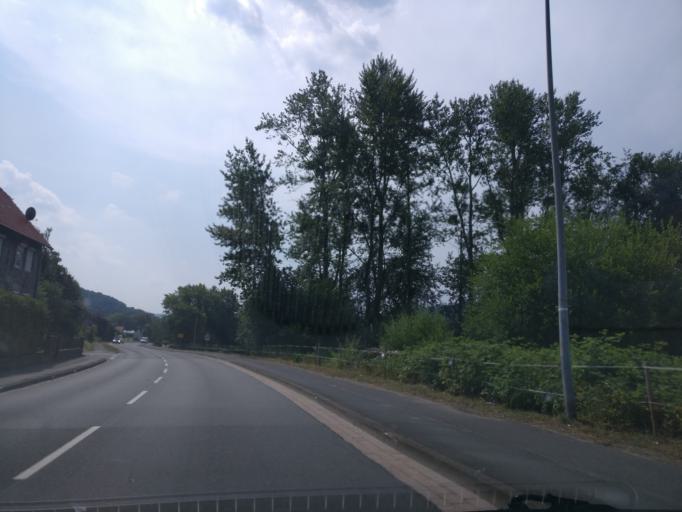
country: DE
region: Lower Saxony
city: Hannoversch Munden
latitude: 51.4341
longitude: 9.6410
